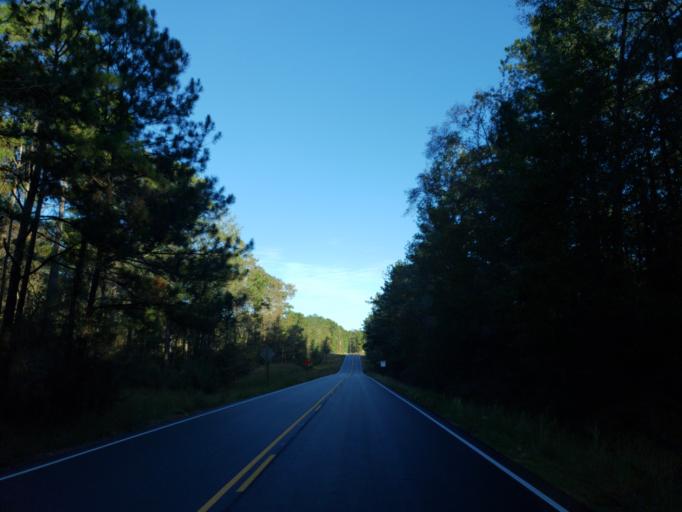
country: US
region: Mississippi
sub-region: Perry County
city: Richton
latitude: 31.3500
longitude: -88.7835
